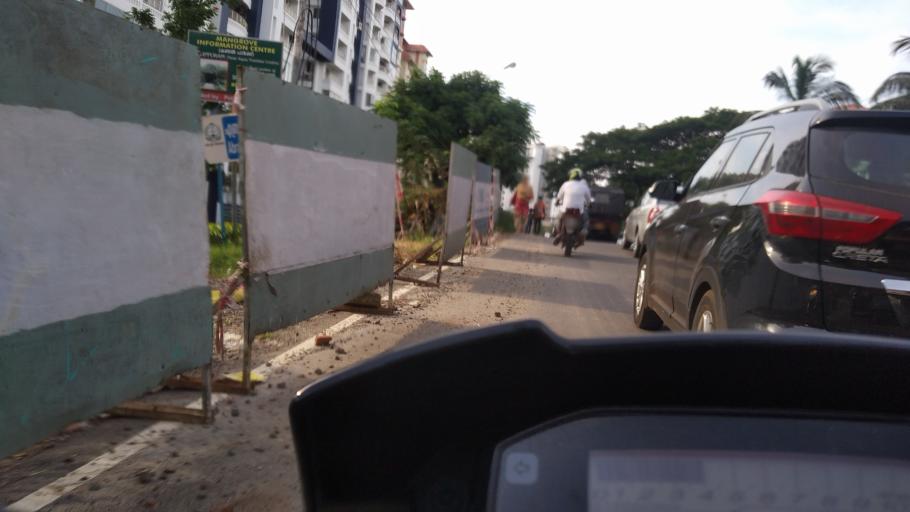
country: IN
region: Kerala
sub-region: Ernakulam
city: Cochin
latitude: 9.9864
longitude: 76.2726
